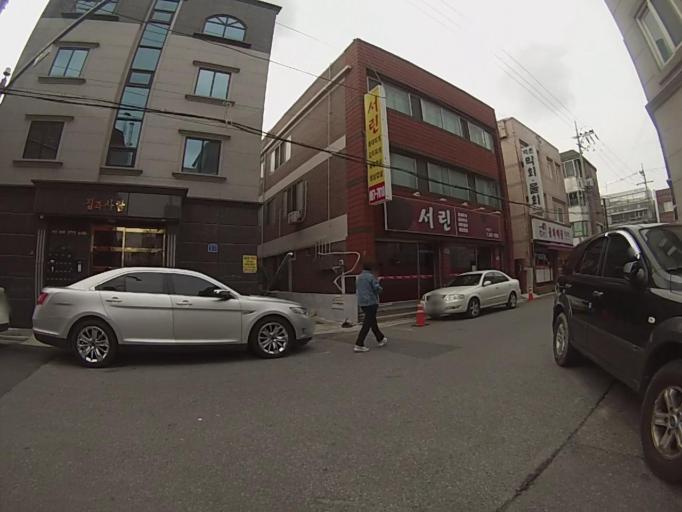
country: KR
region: Daejeon
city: Songgang-dong
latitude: 36.3617
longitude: 127.3540
